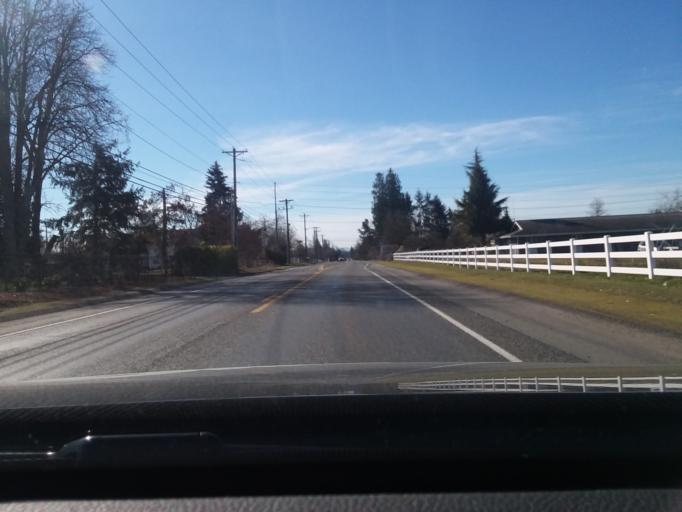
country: US
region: Washington
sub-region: Pierce County
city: Midland
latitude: 47.1712
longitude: -122.3890
